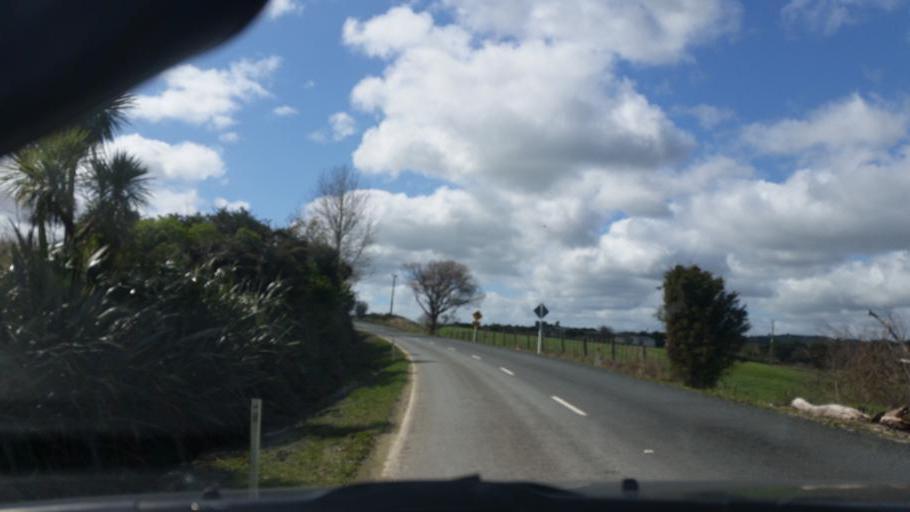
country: NZ
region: Auckland
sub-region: Auckland
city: Wellsford
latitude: -36.1536
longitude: 174.4986
